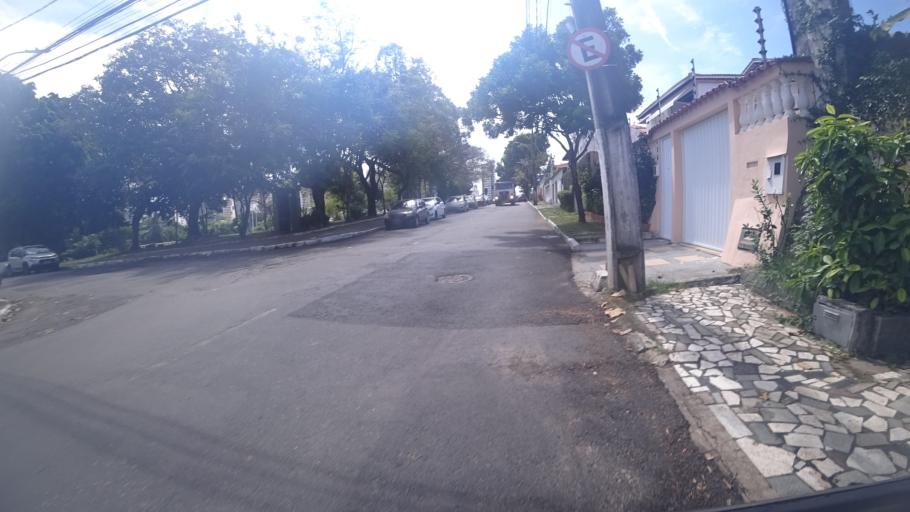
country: BR
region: Bahia
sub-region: Salvador
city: Salvador
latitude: -12.9924
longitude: -38.4580
